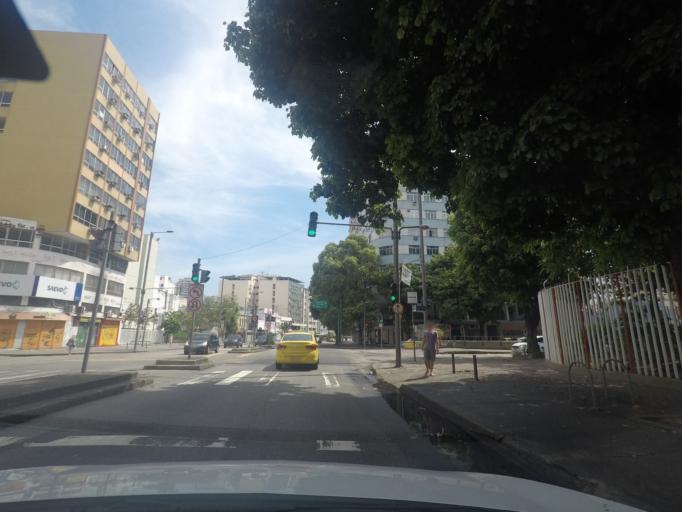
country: BR
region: Rio de Janeiro
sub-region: Rio De Janeiro
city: Rio de Janeiro
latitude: -22.9266
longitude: -43.2353
